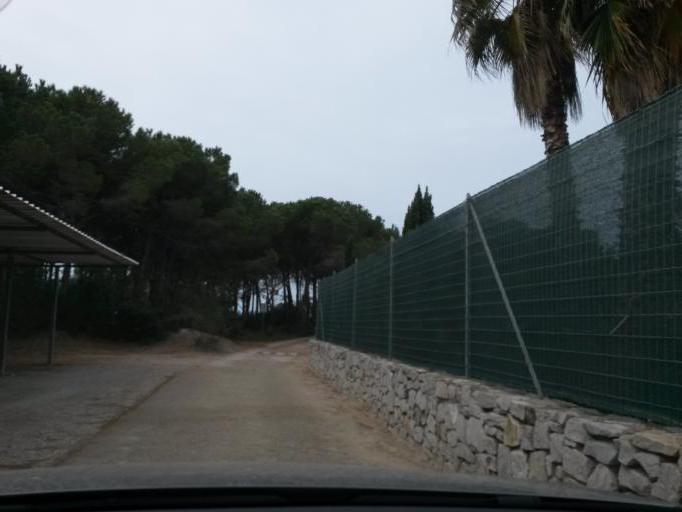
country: IT
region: Tuscany
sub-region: Provincia di Livorno
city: Capoliveri
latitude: 42.7327
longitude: 10.3699
